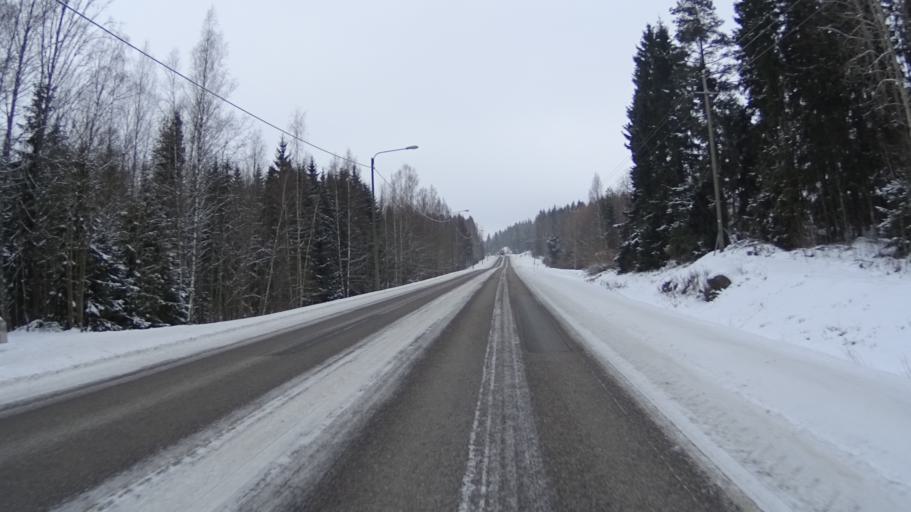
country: FI
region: Uusimaa
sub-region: Helsinki
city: Vihti
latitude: 60.3557
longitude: 24.1795
